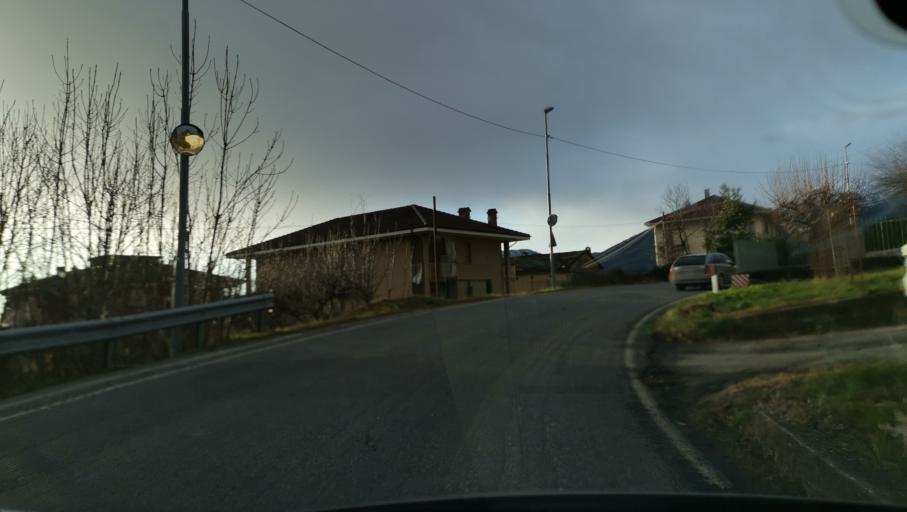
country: IT
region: Piedmont
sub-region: Provincia di Torino
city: Coazze
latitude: 45.0549
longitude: 7.3120
